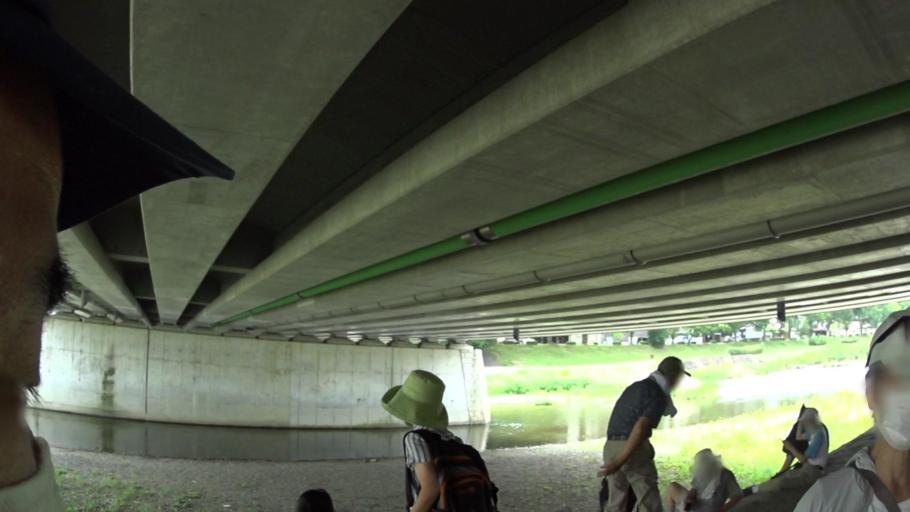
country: JP
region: Kyoto
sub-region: Kyoto-shi
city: Kamigyo-ku
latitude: 35.0532
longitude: 135.7563
